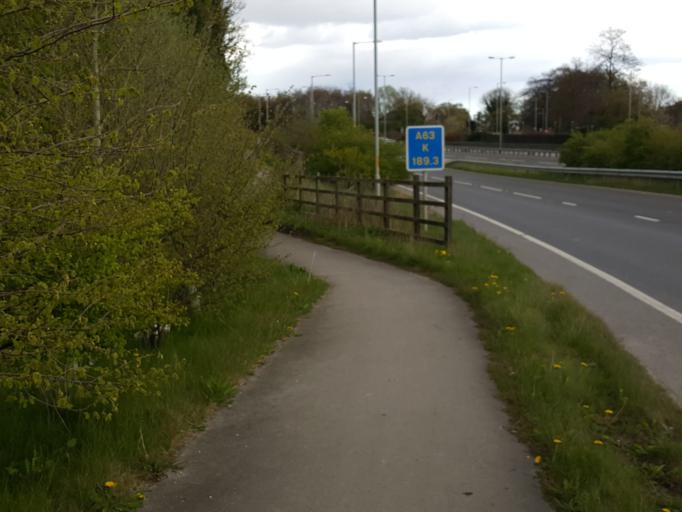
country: GB
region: England
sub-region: East Riding of Yorkshire
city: North Ferriby
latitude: 53.7247
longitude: -0.5189
